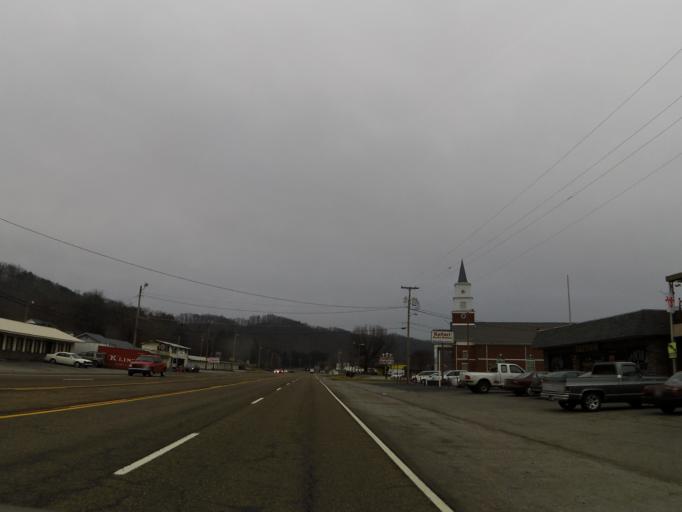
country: US
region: Tennessee
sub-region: Anderson County
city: Clinton
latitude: 36.0746
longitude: -84.1328
